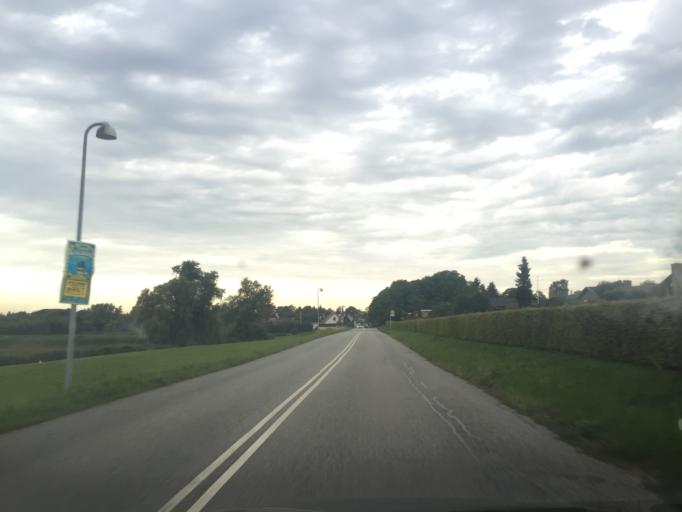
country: DK
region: Zealand
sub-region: Roskilde Kommune
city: Gundsomagle
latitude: 55.7339
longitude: 12.1603
